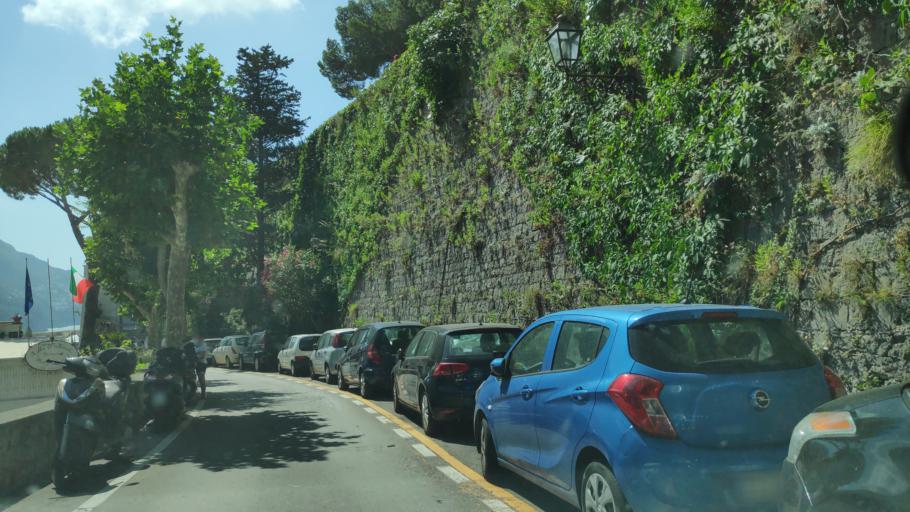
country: IT
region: Campania
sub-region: Provincia di Salerno
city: Positano
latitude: 40.6293
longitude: 14.4829
